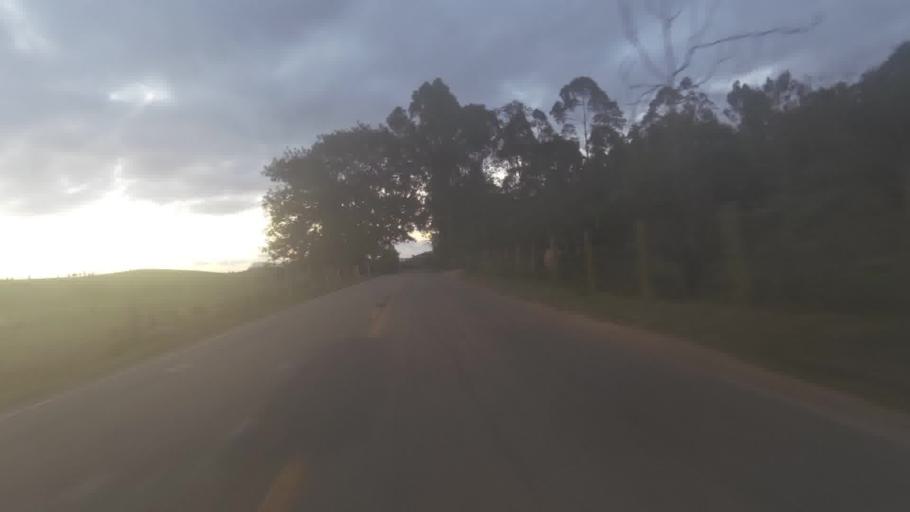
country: BR
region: Espirito Santo
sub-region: Itapemirim
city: Itapemirim
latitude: -20.9707
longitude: -40.8692
